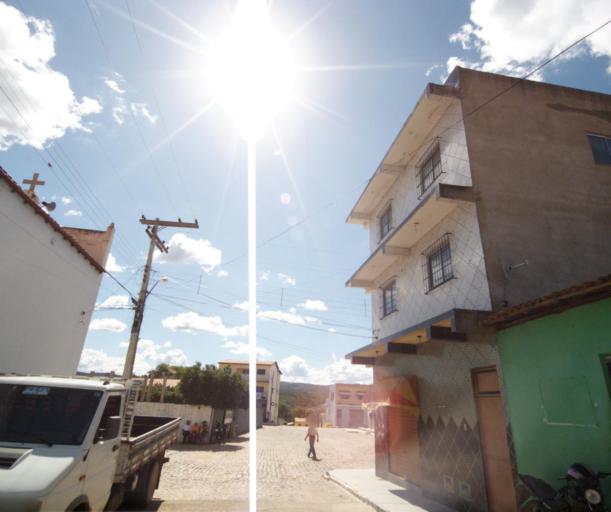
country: BR
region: Bahia
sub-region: Pocoes
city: Pocoes
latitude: -14.2414
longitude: -40.7726
